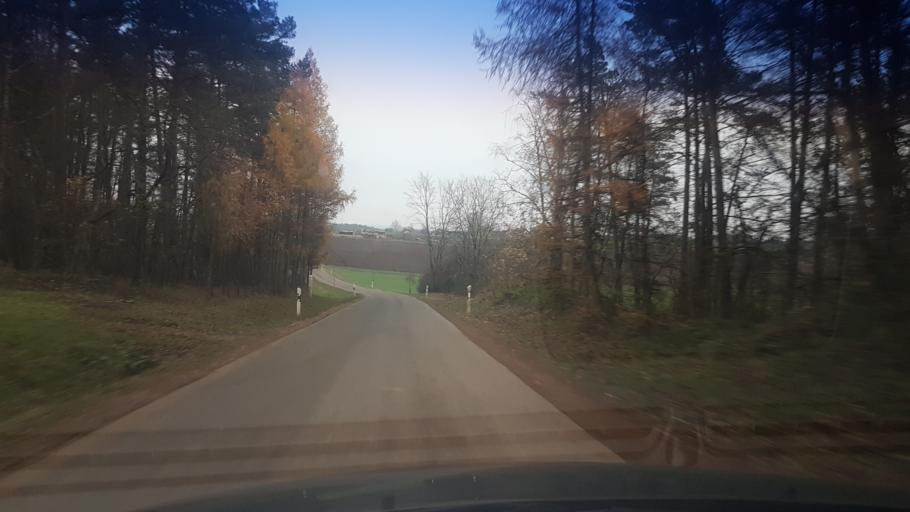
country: DE
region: Bavaria
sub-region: Upper Franconia
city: Kasendorf
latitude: 50.0409
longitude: 11.2892
